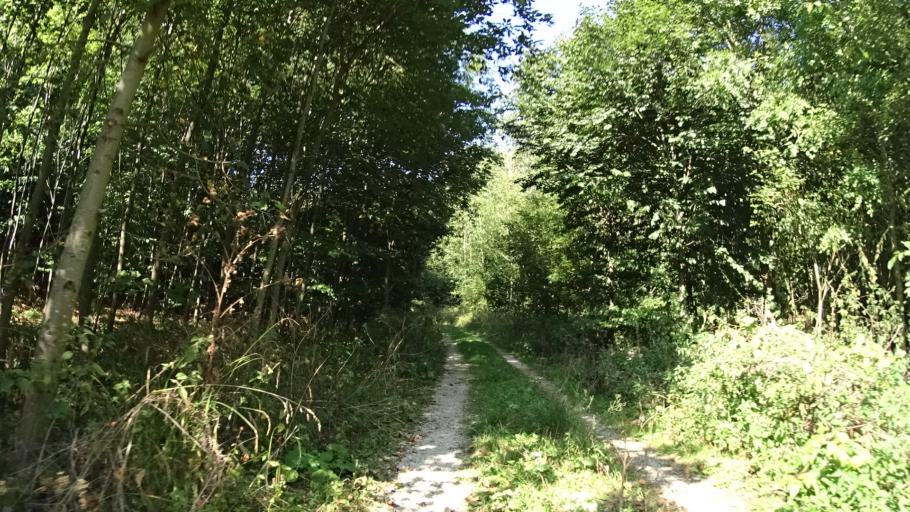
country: DE
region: Bavaria
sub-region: Upper Bavaria
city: Walting
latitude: 48.9518
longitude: 11.3556
